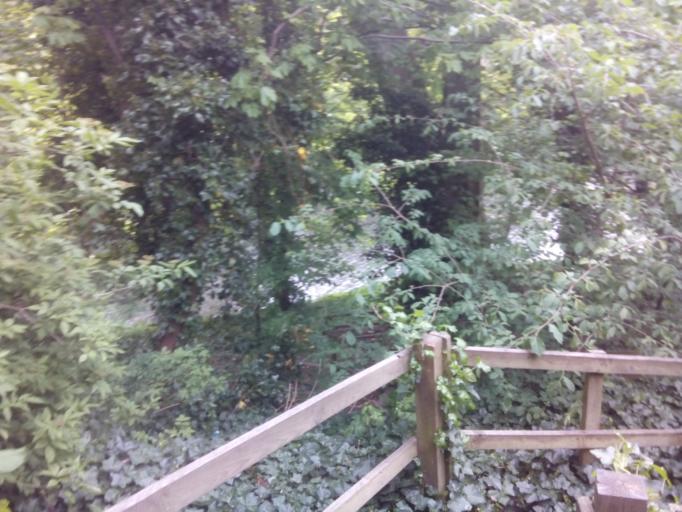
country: GB
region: England
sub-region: County Durham
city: Durham
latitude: 54.7730
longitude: -1.5720
